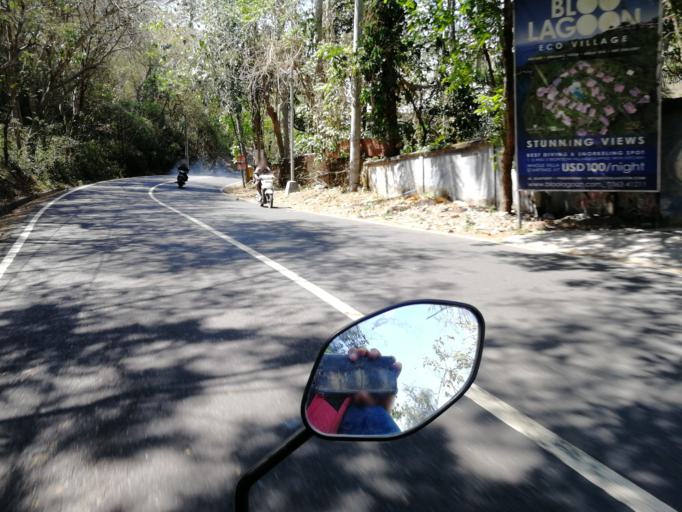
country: ID
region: Bali
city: Padangbai
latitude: -8.5279
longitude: 115.5046
